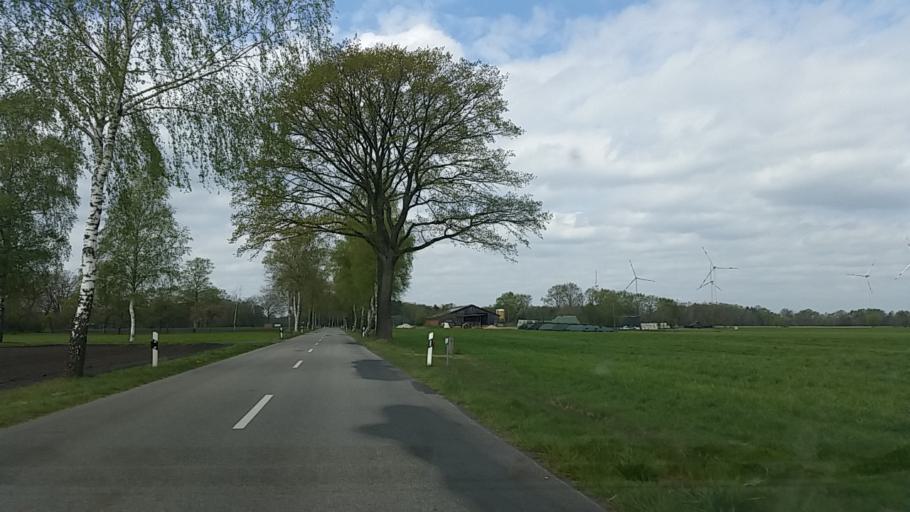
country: DE
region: Lower Saxony
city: Konigsmoor
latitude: 53.1967
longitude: 9.7157
